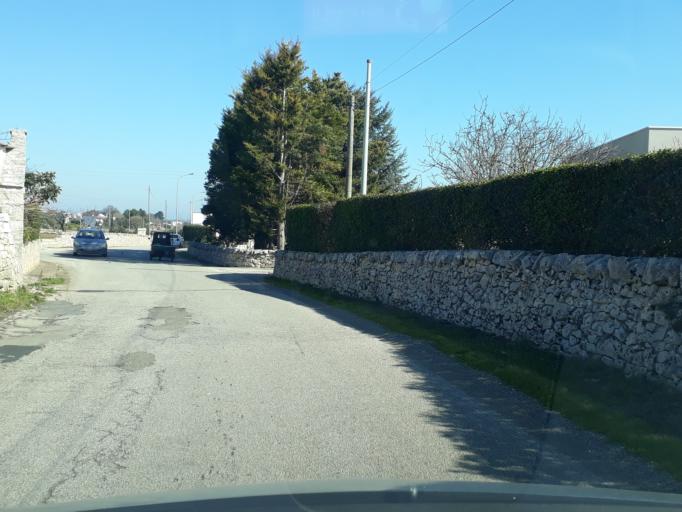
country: IT
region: Apulia
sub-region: Provincia di Taranto
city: Martina Franca
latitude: 40.7258
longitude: 17.3511
